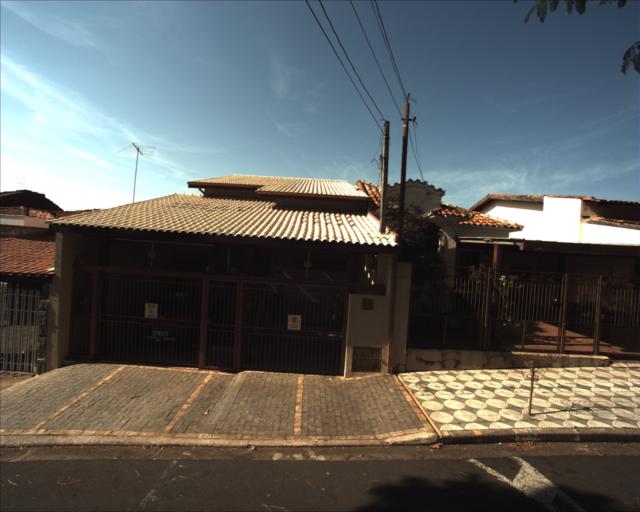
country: BR
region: Sao Paulo
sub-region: Sorocaba
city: Sorocaba
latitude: -23.4839
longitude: -47.4403
